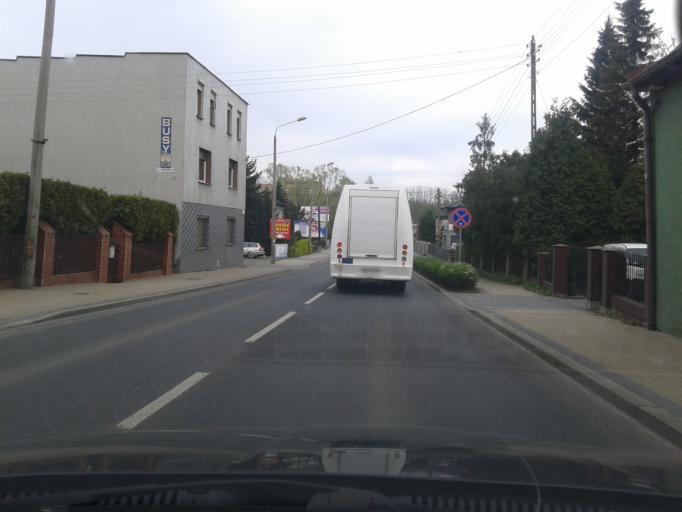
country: PL
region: Silesian Voivodeship
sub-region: Rybnik
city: Rybnik
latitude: 50.0892
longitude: 18.5368
